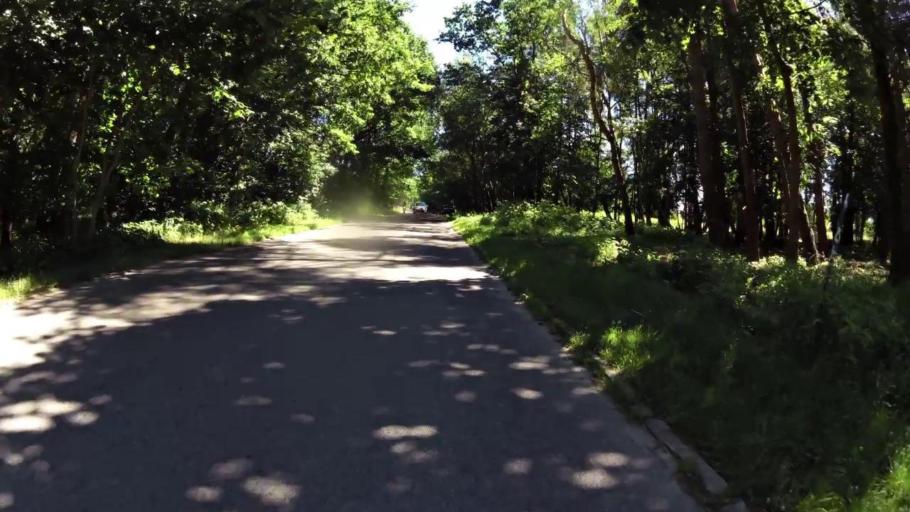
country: PL
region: West Pomeranian Voivodeship
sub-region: Powiat gryficki
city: Rewal
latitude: 54.0902
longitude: 15.0473
